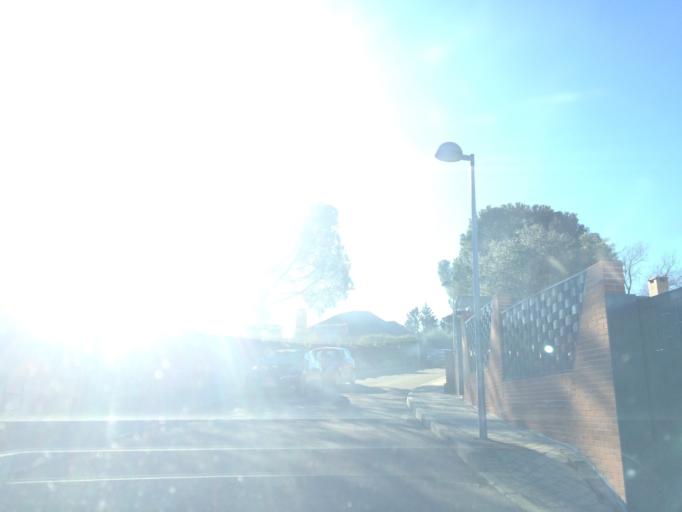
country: ES
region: Madrid
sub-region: Provincia de Madrid
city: Tres Cantos
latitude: 40.6113
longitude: -3.6898
